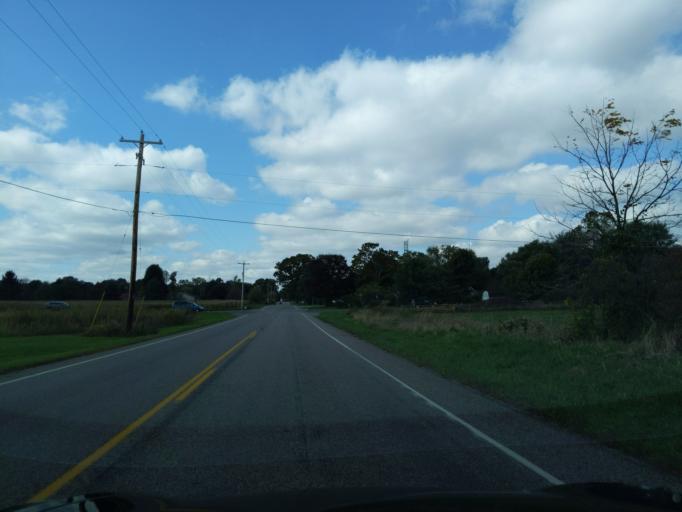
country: US
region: Michigan
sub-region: Eaton County
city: Potterville
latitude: 42.5676
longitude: -84.7674
